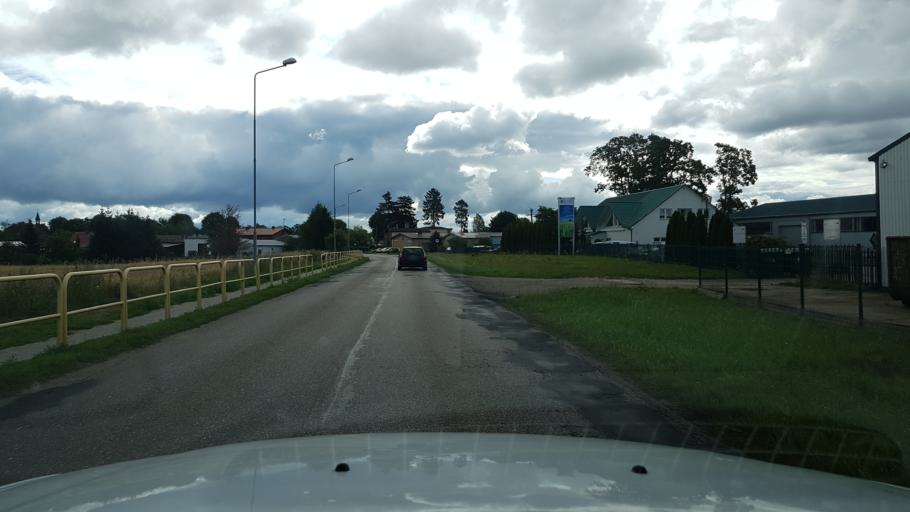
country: PL
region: West Pomeranian Voivodeship
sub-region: Powiat swidwinski
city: Rabino
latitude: 53.7746
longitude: 15.9632
